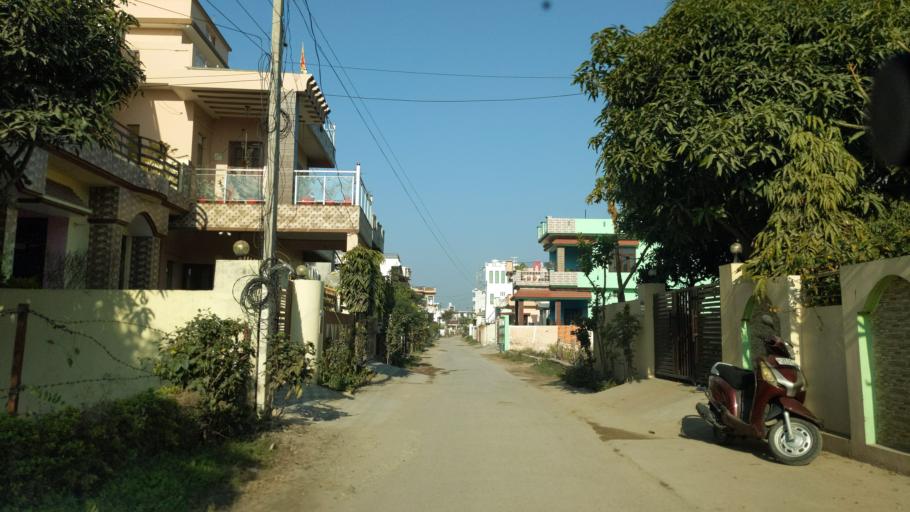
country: IN
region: Uttarakhand
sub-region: Naini Tal
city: Haldwani
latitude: 29.2066
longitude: 79.4973
